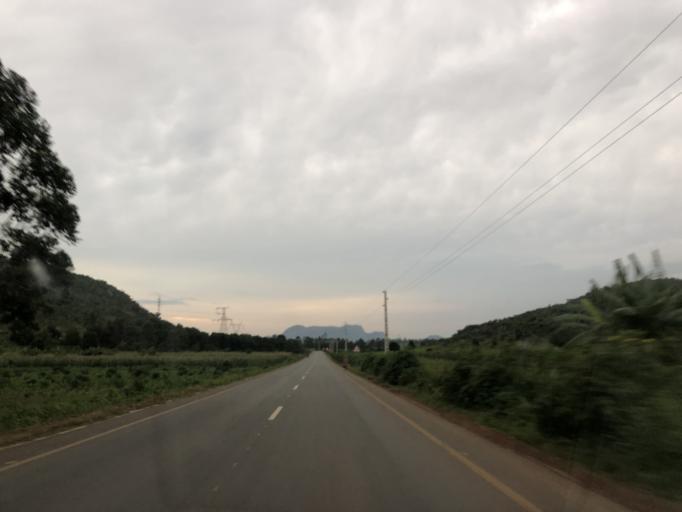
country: AO
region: Cuanza Sul
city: Uacu Cungo
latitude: -11.3295
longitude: 15.0956
